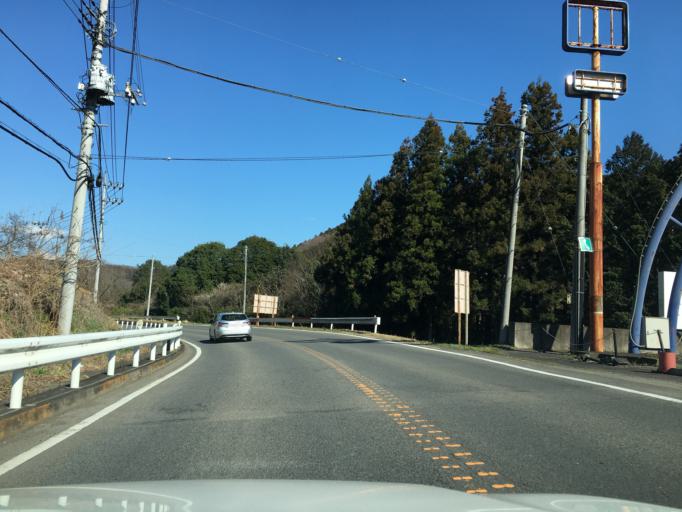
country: JP
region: Tochigi
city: Motegi
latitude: 36.5475
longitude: 140.2320
